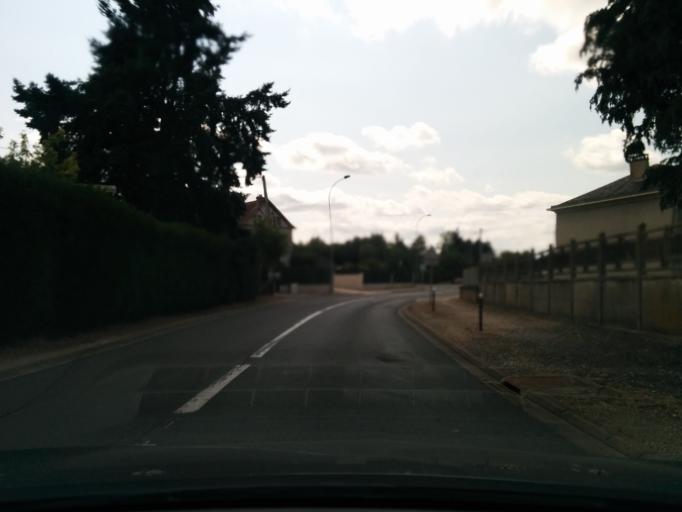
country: FR
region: Centre
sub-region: Departement du Cher
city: Henrichemont
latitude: 47.3620
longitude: 2.4334
